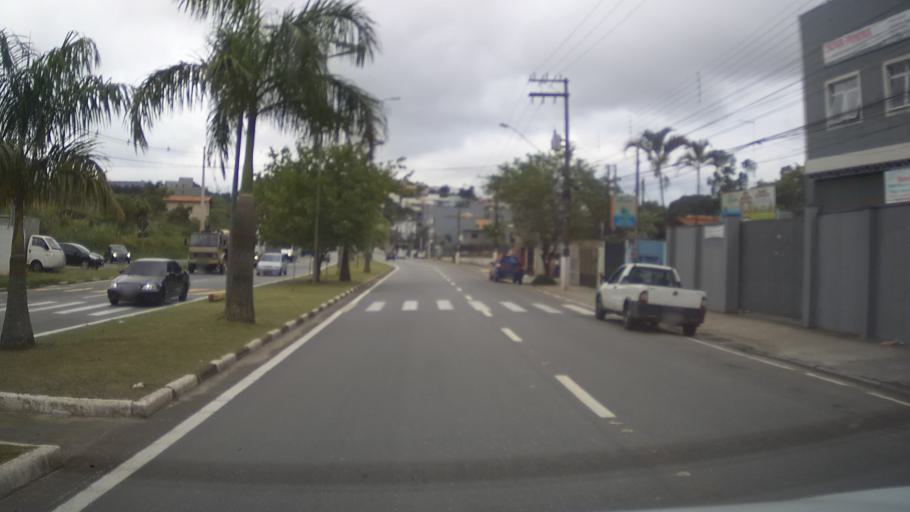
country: BR
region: Sao Paulo
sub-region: Aruja
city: Aruja
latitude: -23.4133
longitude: -46.3245
